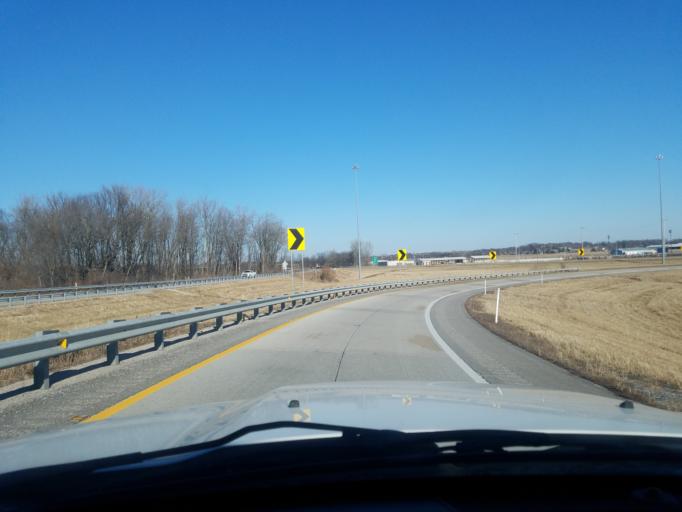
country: US
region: Kentucky
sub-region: Henderson County
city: Henderson
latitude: 37.8122
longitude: -87.5662
